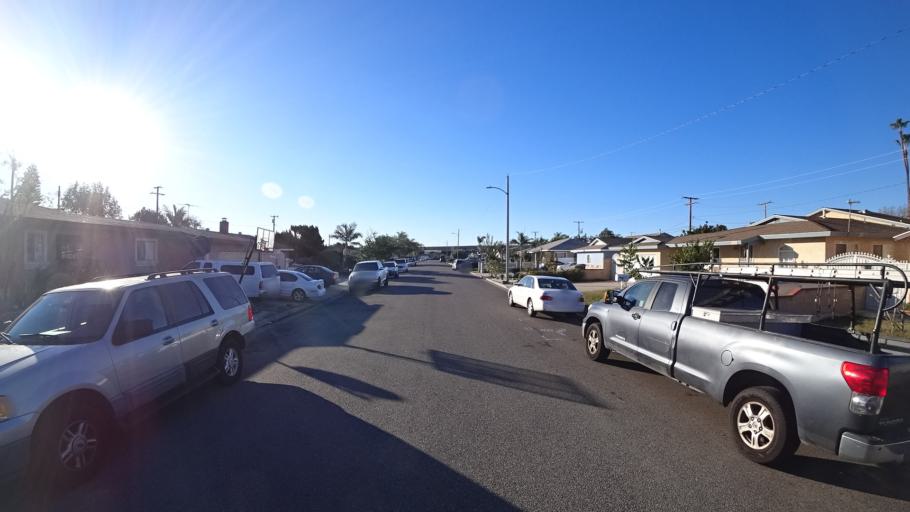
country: US
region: California
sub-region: Orange County
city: Midway City
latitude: 33.7698
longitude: -117.9751
